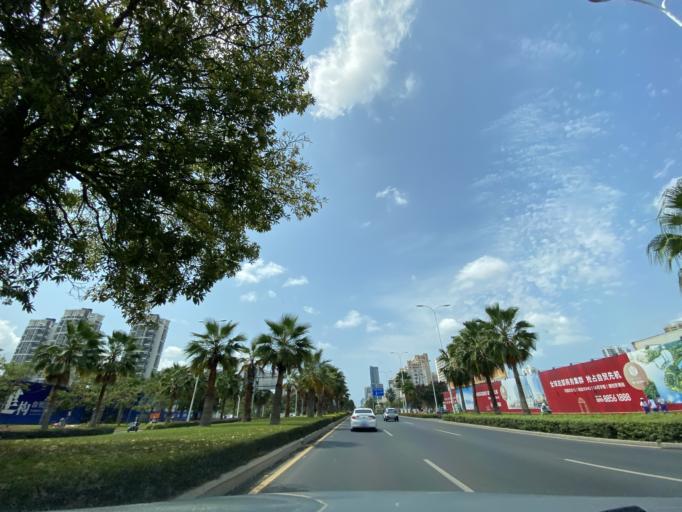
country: CN
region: Hainan
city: Sanya
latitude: 18.2830
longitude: 109.5158
